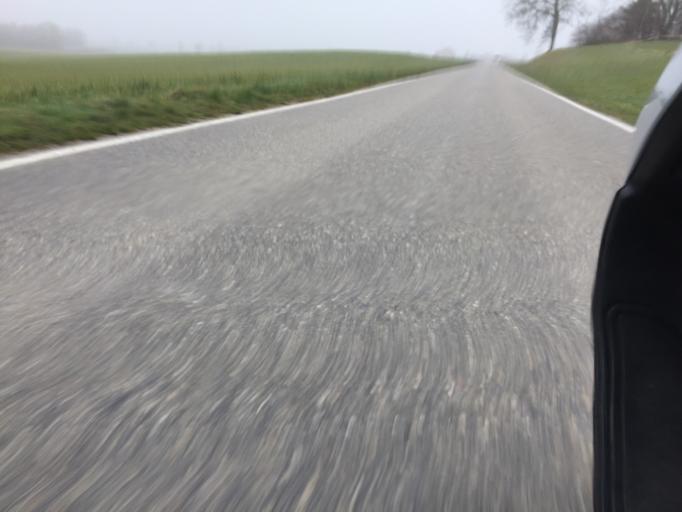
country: CH
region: Bern
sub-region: Seeland District
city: Grossaffoltern
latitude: 47.0838
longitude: 7.3821
